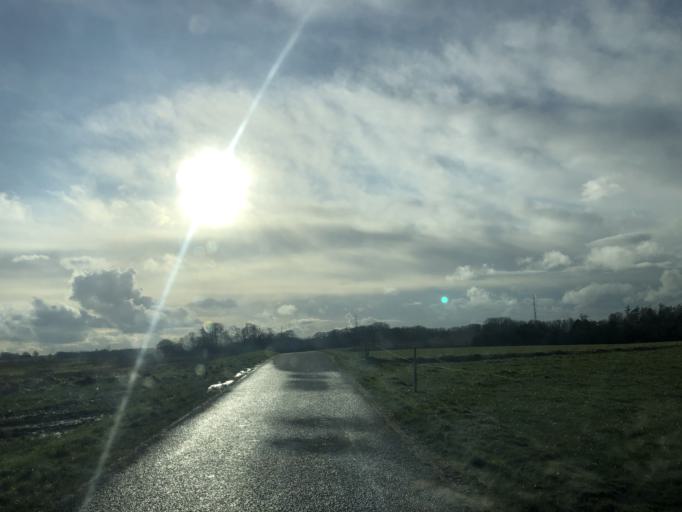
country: DK
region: North Denmark
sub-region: Vesthimmerland Kommune
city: Alestrup
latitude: 56.6439
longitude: 9.6263
